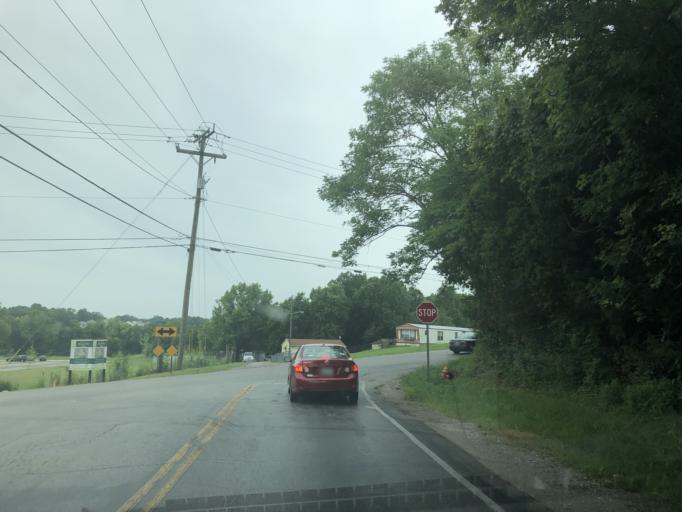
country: US
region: Tennessee
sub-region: Williamson County
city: Nolensville
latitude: 36.0286
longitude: -86.6726
